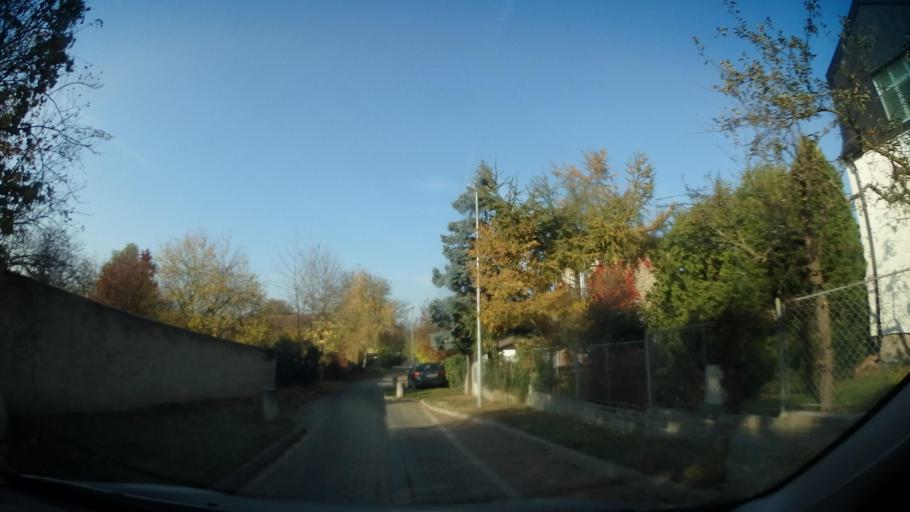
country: CZ
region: Praha
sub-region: Praha 14
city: Dolni Pocernice
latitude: 50.0897
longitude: 14.5797
